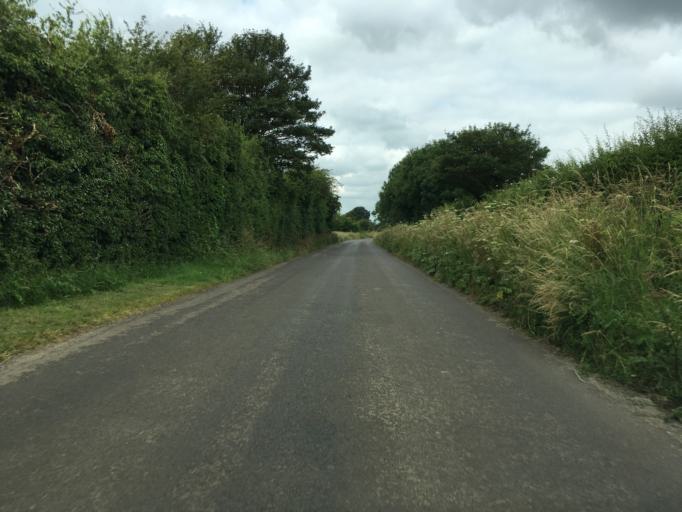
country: GB
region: England
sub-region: Oxfordshire
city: Chipping Norton
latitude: 51.9257
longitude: -1.5612
